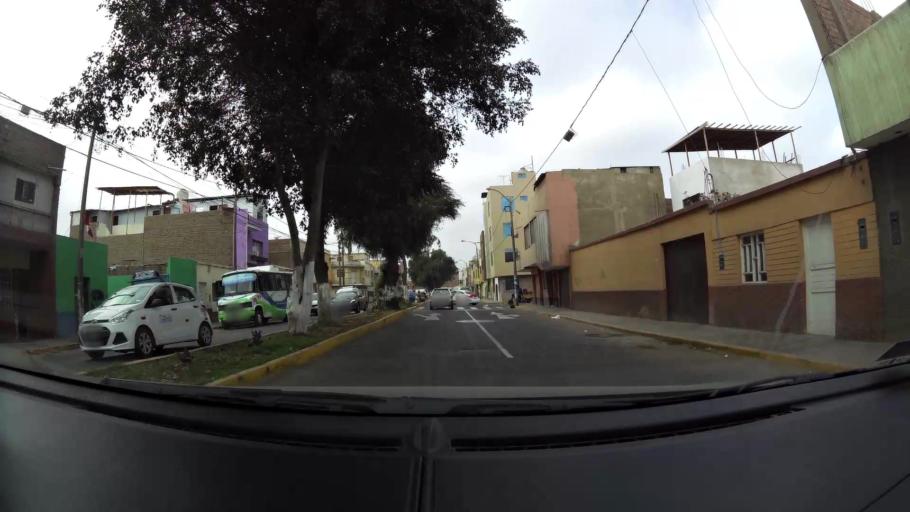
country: PE
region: La Libertad
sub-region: Provincia de Trujillo
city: Trujillo
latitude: -8.1016
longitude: -79.0185
